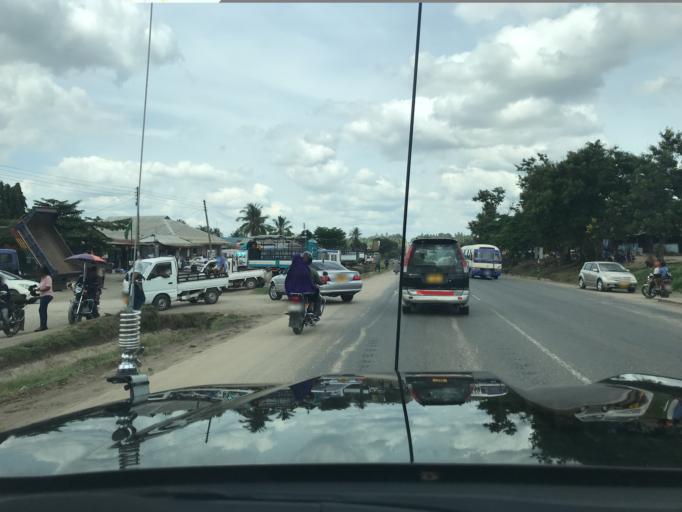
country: TZ
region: Pwani
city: Kibaha
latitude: -6.7644
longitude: 38.9527
